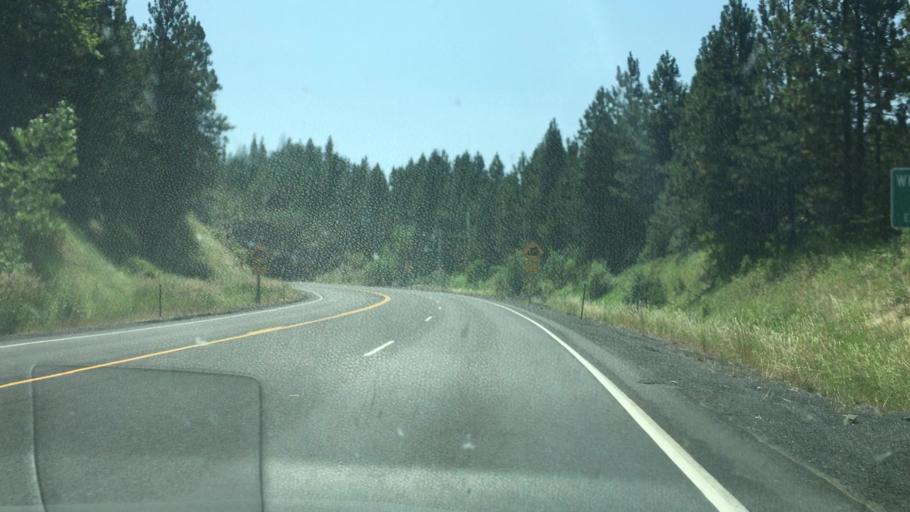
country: US
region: Idaho
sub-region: Idaho County
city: Grangeville
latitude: 45.8485
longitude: -116.2395
